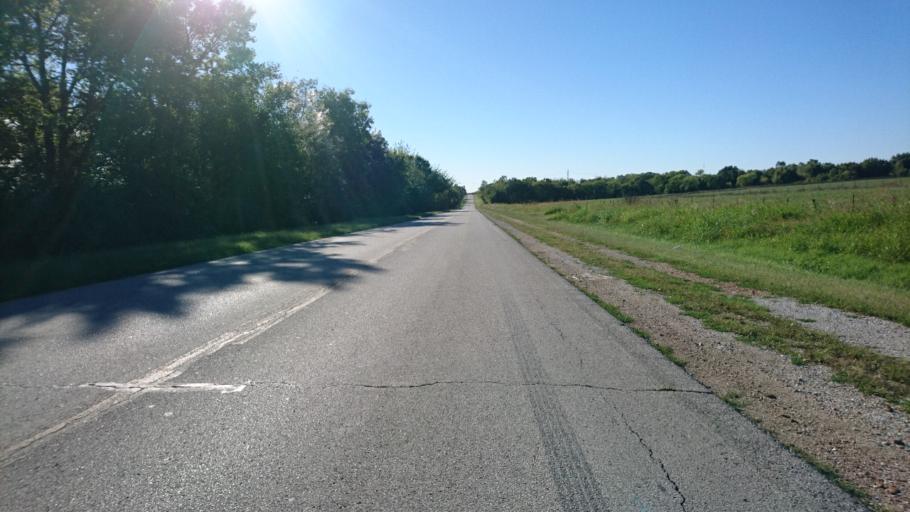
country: US
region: Missouri
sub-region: Jasper County
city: Carthage
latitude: 37.1731
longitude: -94.3700
